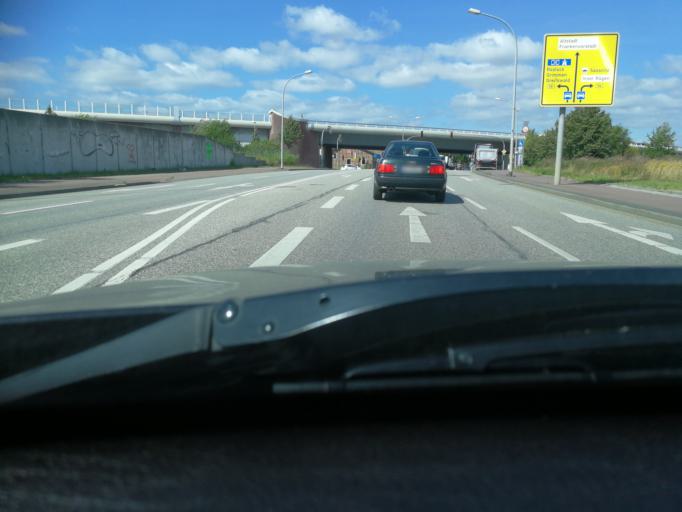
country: DE
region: Mecklenburg-Vorpommern
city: Stralsund
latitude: 54.2982
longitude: 13.0924
